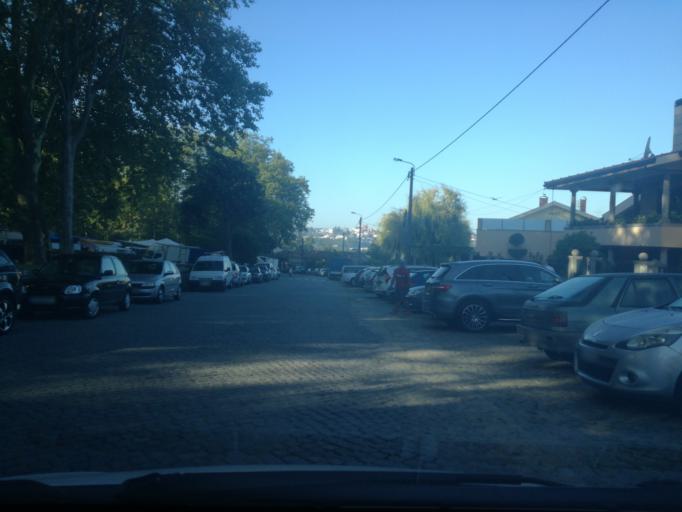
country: PT
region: Porto
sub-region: Maia
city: Leca do Bailio
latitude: 41.2122
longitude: -8.6158
